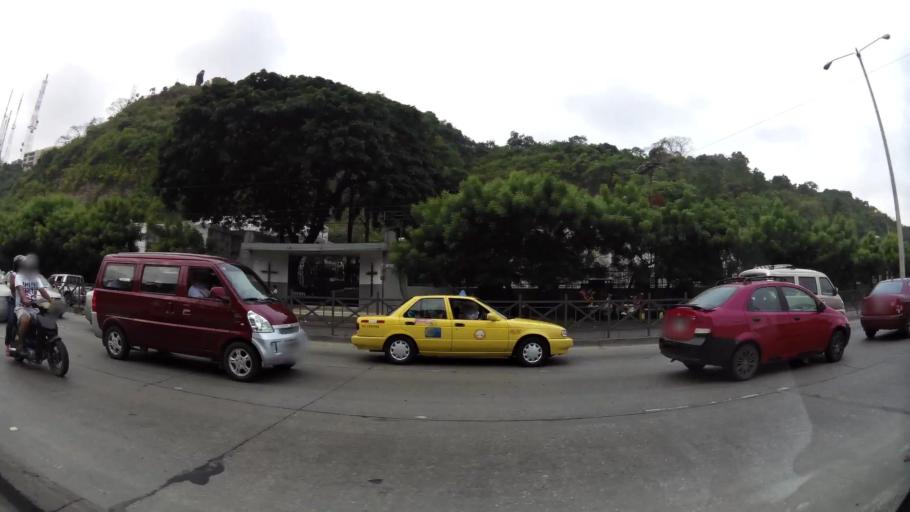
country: EC
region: Guayas
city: Eloy Alfaro
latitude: -2.1789
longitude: -79.8854
